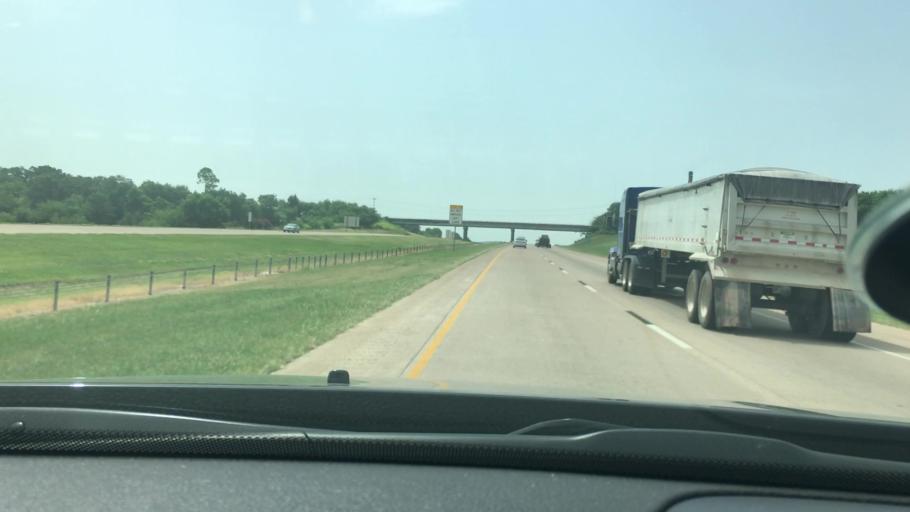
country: US
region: Oklahoma
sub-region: Garvin County
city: Pauls Valley
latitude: 34.7274
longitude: -97.2553
